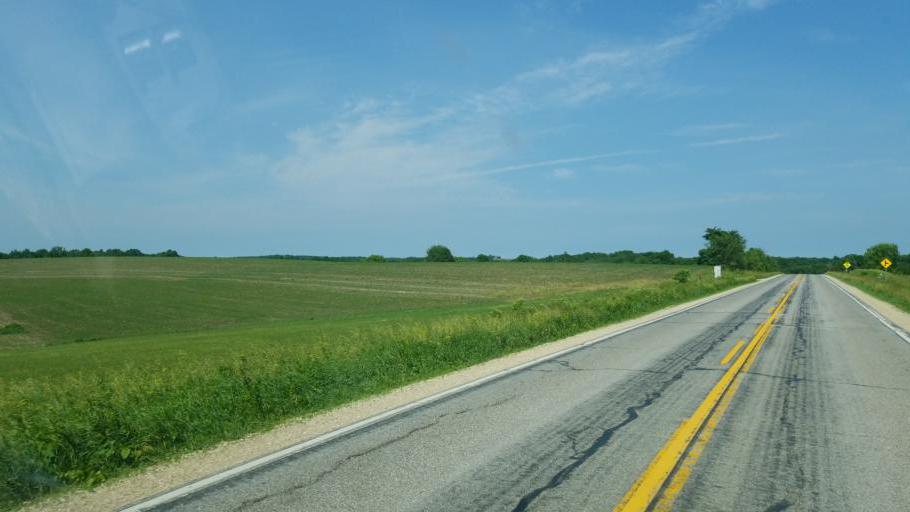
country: US
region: Wisconsin
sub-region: Vernon County
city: Hillsboro
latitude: 43.5977
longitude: -90.4765
